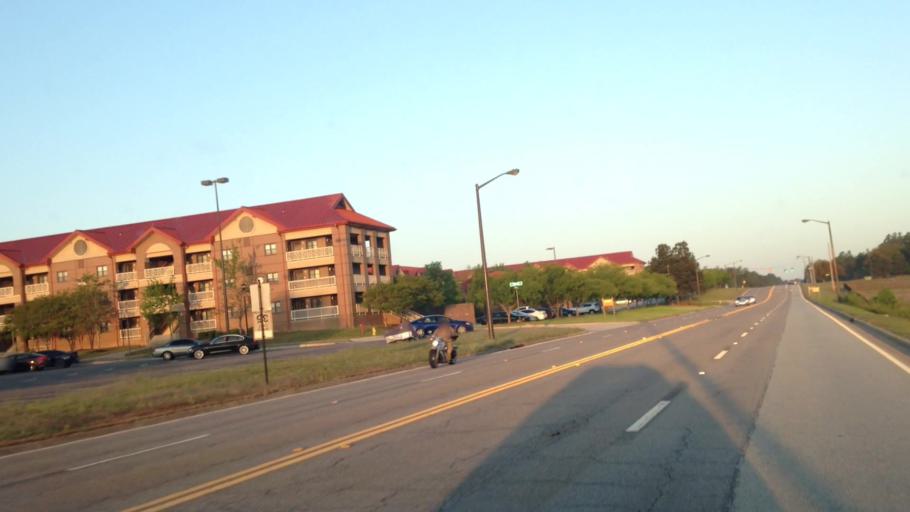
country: US
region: Georgia
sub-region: Columbia County
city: Grovetown
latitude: 33.4256
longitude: -82.1593
